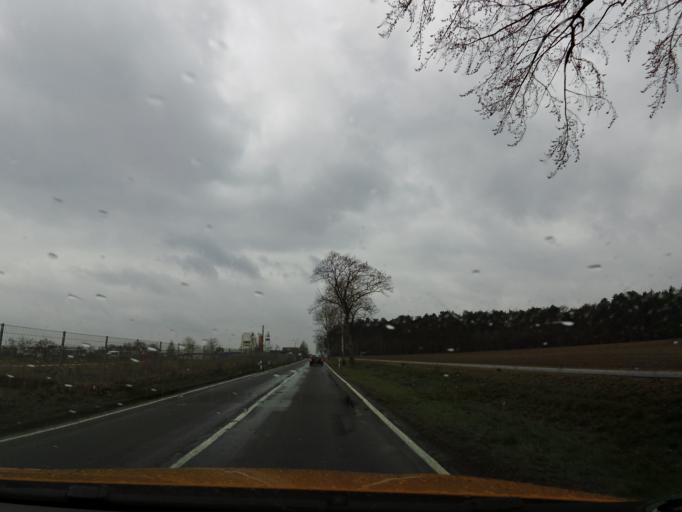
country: DE
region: Brandenburg
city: Ziesar
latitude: 52.2541
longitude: 12.2640
